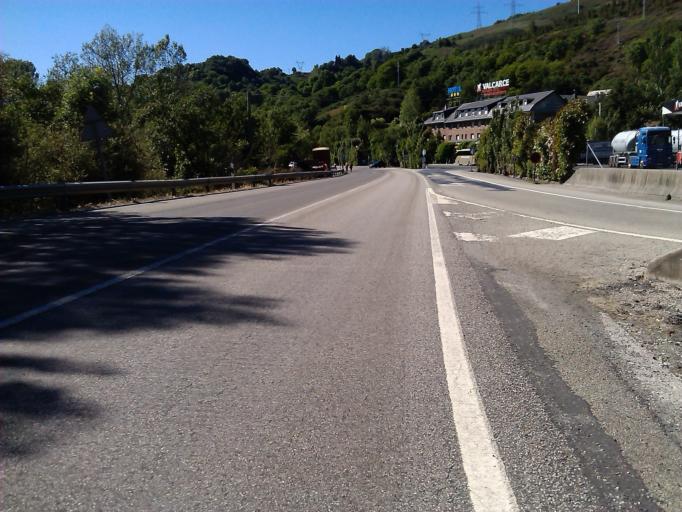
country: ES
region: Castille and Leon
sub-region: Provincia de Leon
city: Vega de Valcarce
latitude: 42.6581
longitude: -6.9141
